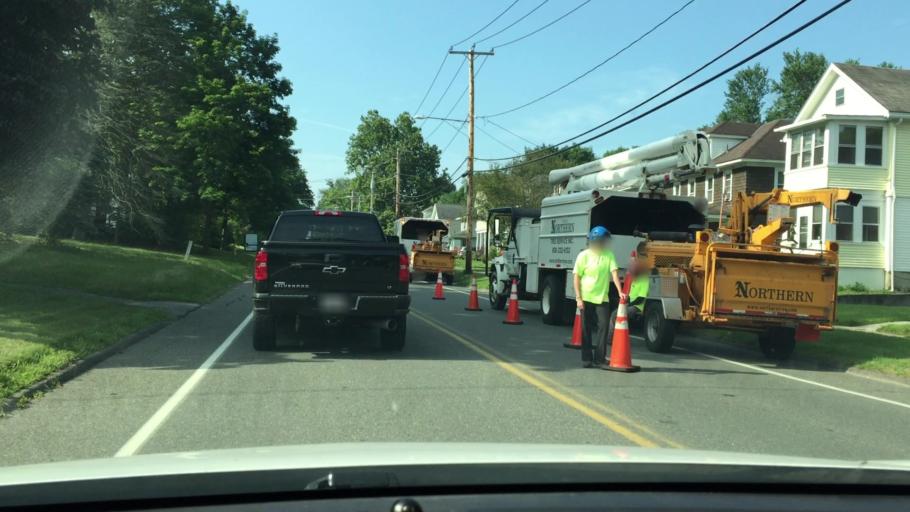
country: US
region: Massachusetts
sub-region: Berkshire County
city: Pittsfield
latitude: 42.4425
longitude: -73.2349
